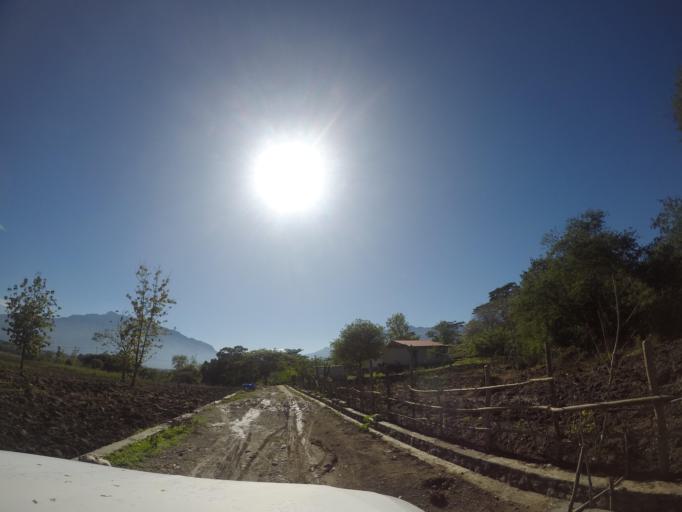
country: TL
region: Bobonaro
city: Maliana
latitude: -8.9978
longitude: 125.1907
